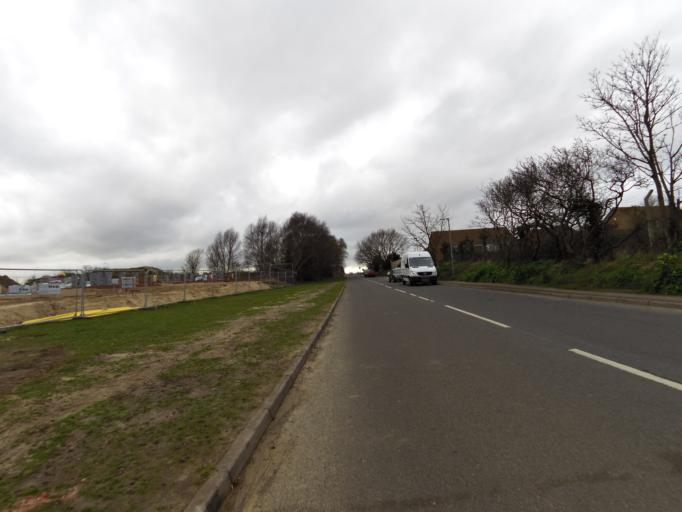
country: GB
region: England
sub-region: Norfolk
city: Hopton on Sea
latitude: 52.5410
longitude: 1.7210
